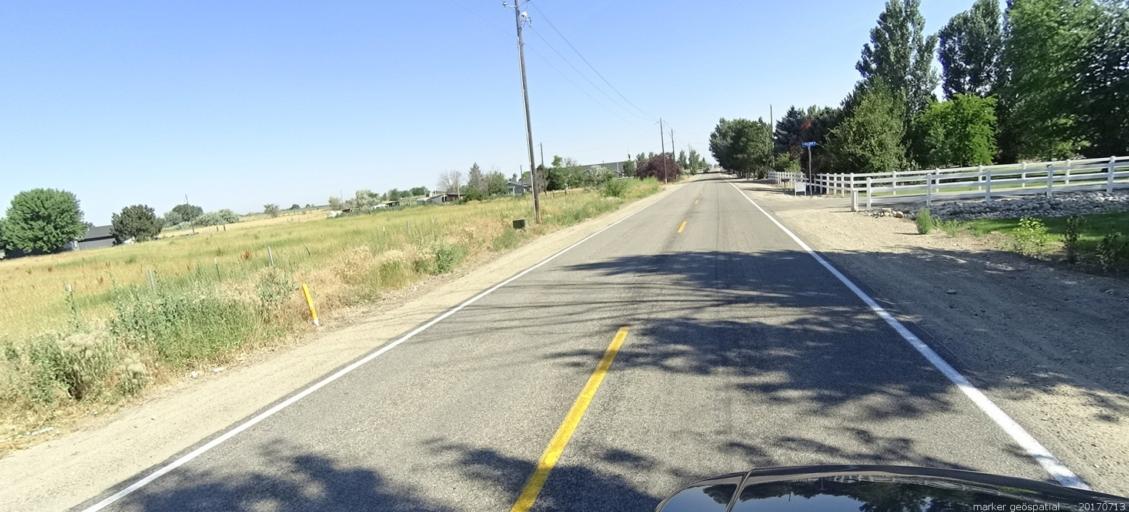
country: US
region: Idaho
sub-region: Ada County
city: Kuna
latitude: 43.5229
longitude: -116.4138
